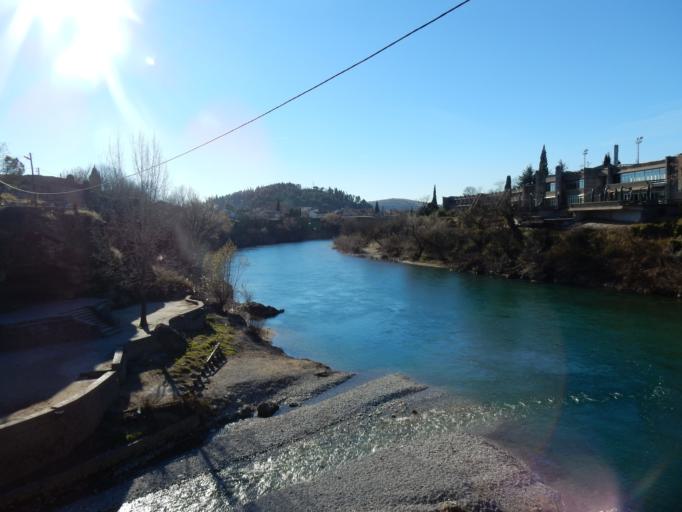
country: ME
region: Podgorica
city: Podgorica
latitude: 42.4396
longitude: 19.2585
